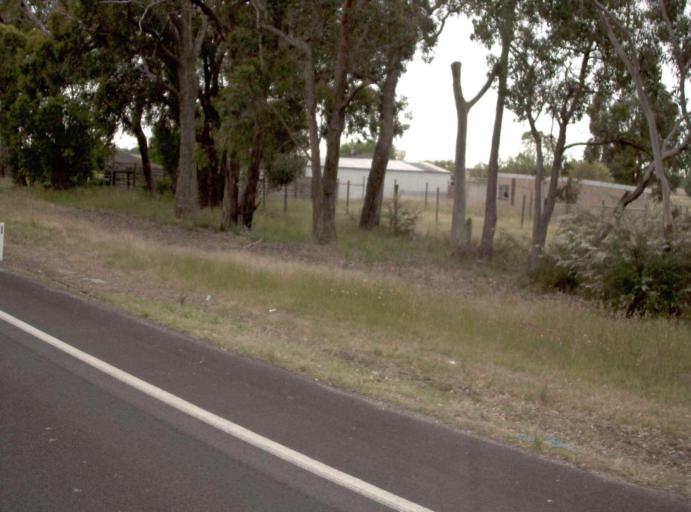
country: AU
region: Victoria
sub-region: Wellington
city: Sale
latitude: -38.3159
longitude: 147.0256
